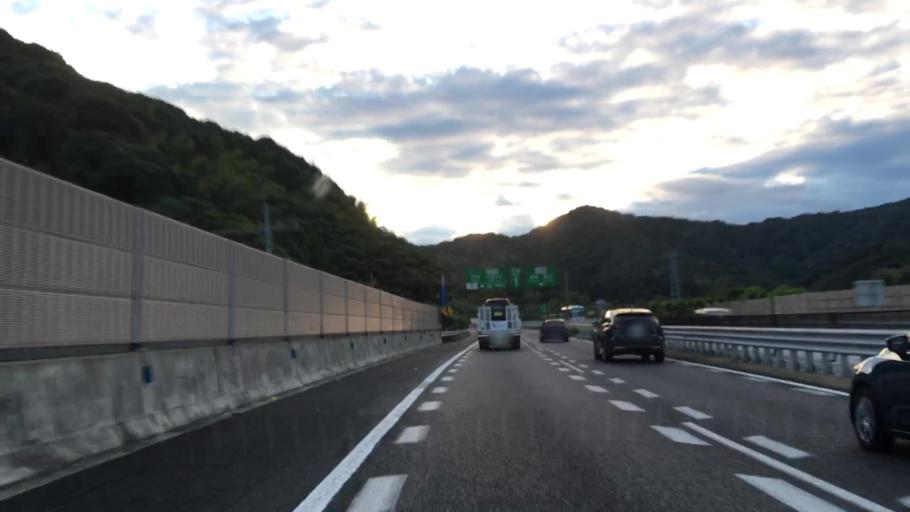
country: JP
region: Yamaguchi
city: Shimonoseki
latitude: 33.9274
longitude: 130.9895
